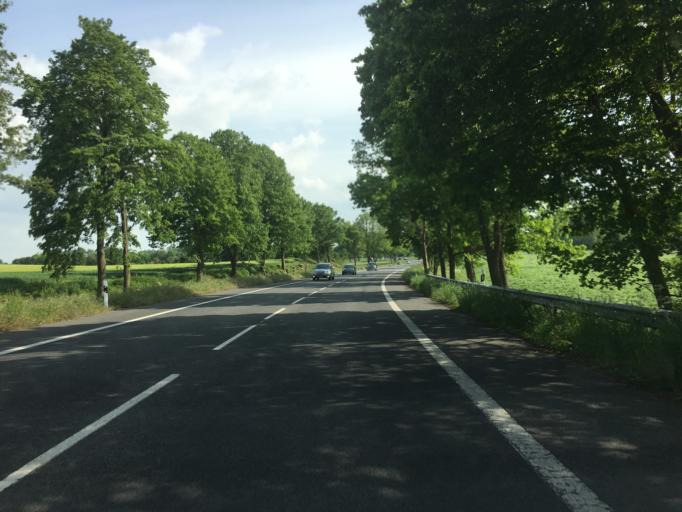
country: DE
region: North Rhine-Westphalia
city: Julich
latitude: 50.9553
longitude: 6.3267
